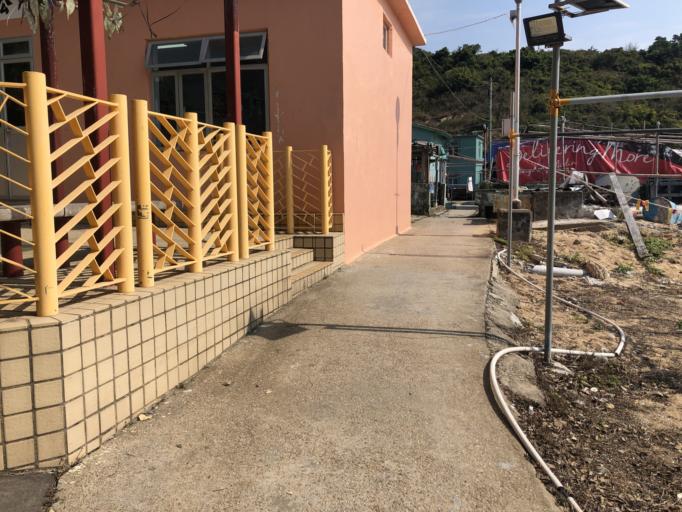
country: HK
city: Sok Kwu Wan
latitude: 22.1654
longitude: 114.2538
